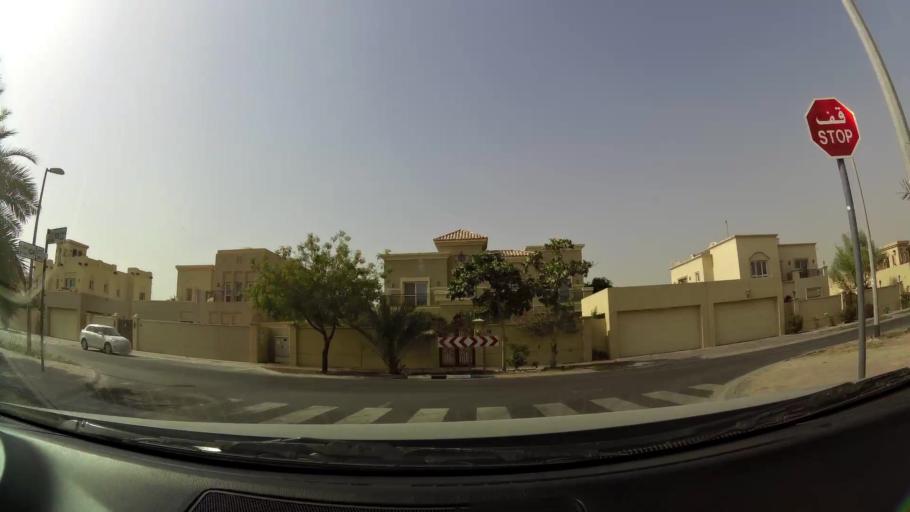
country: AE
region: Ash Shariqah
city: Sharjah
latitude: 25.2634
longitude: 55.4536
